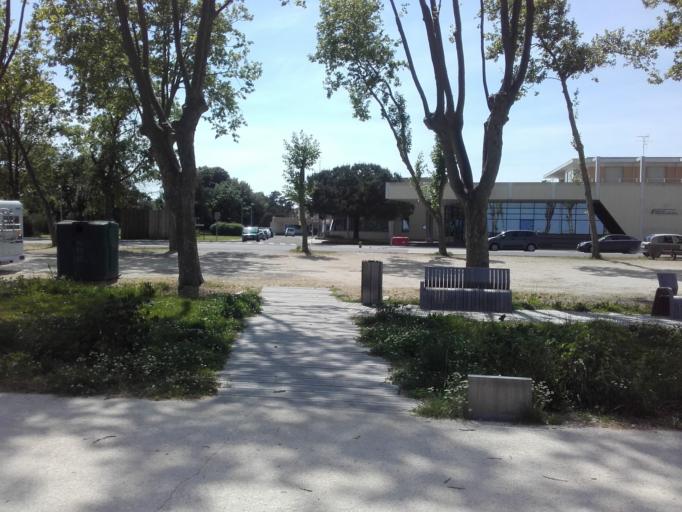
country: FR
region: Aquitaine
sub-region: Departement de la Gironde
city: Pauillac
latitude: 45.1959
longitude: -0.7439
